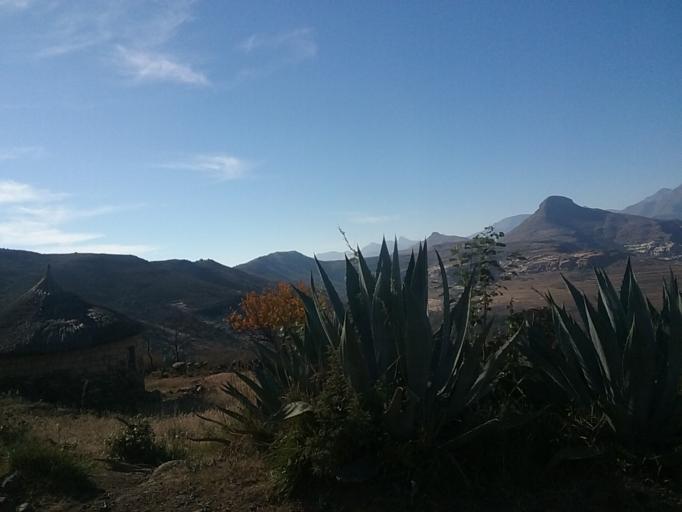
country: LS
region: Berea
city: Teyateyaneng
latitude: -29.2372
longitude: 27.8805
